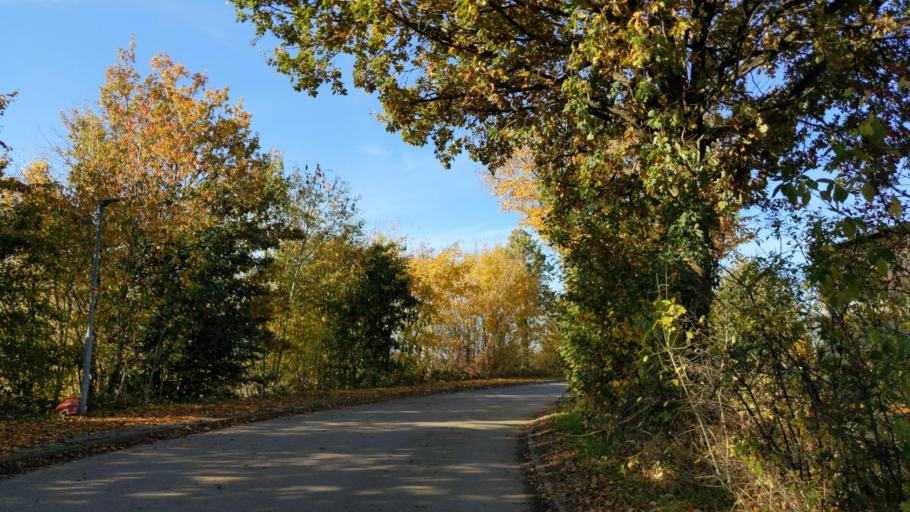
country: DE
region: Schleswig-Holstein
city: Kasseedorf
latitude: 54.1336
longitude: 10.7361
